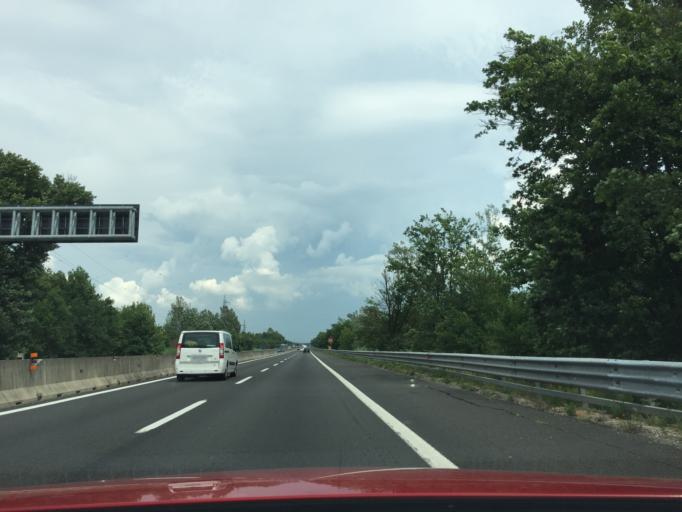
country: IT
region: Tuscany
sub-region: Provincia di Lucca
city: Porcari
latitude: 43.8222
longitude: 10.5998
